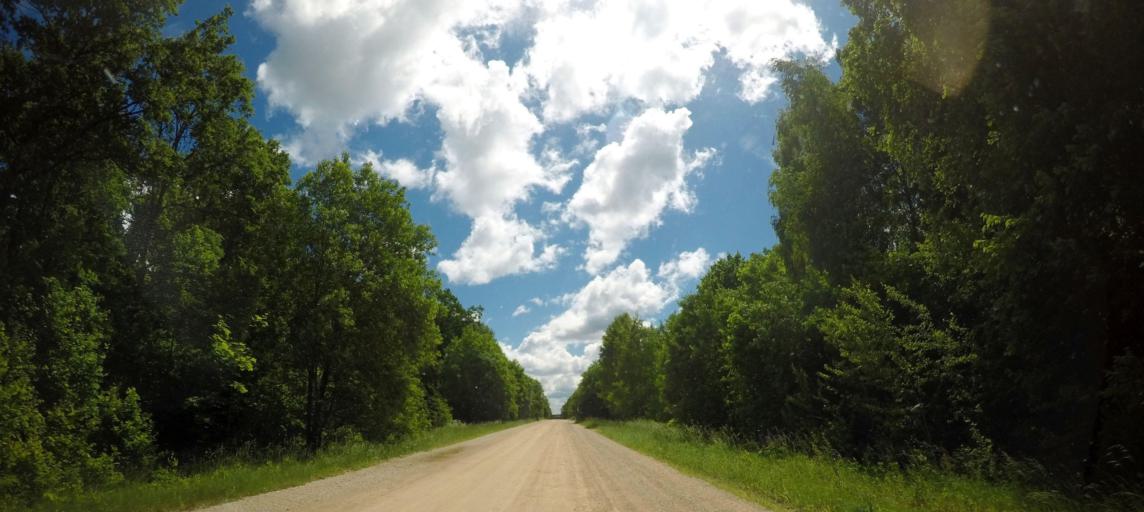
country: BY
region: Grodnenskaya
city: Hal'shany
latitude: 54.2031
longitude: 26.0726
